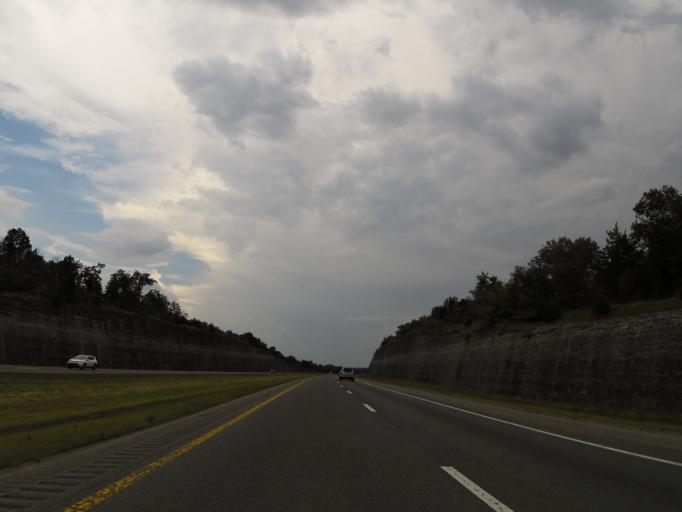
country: US
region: Tennessee
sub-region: Rutherford County
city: Smyrna
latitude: 36.0094
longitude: -86.4277
